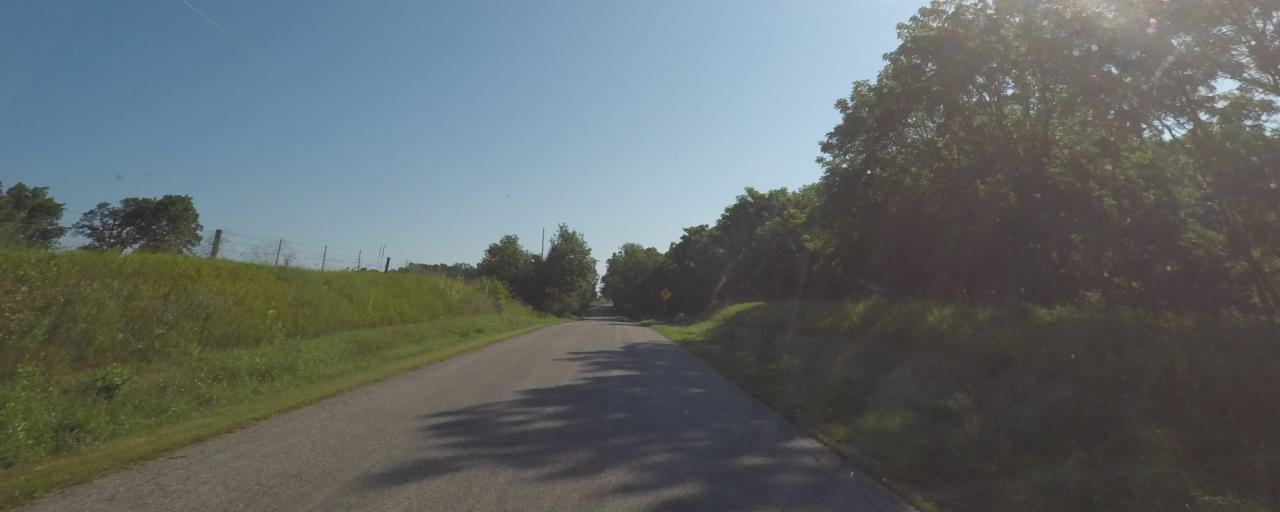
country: US
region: Wisconsin
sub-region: Jefferson County
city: Palmyra
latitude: 42.9165
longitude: -88.5603
